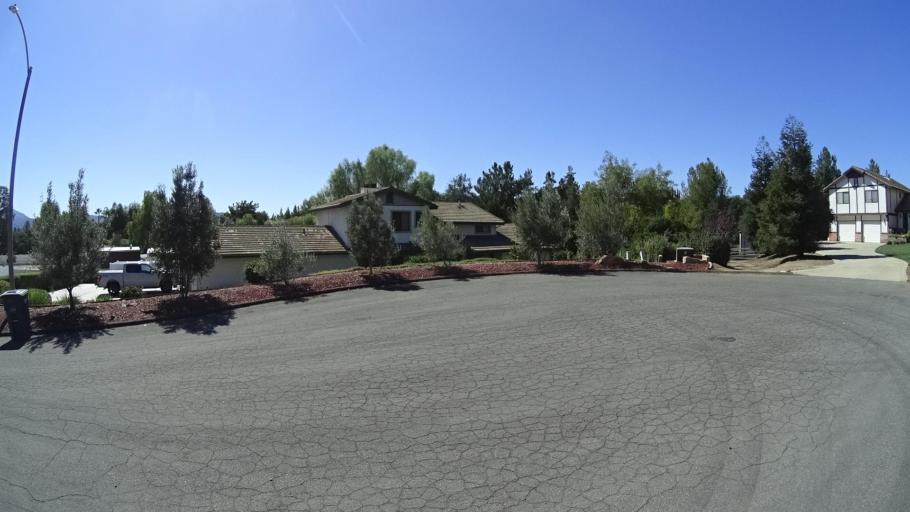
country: US
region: California
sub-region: San Diego County
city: Alpine
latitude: 32.8151
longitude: -116.7797
